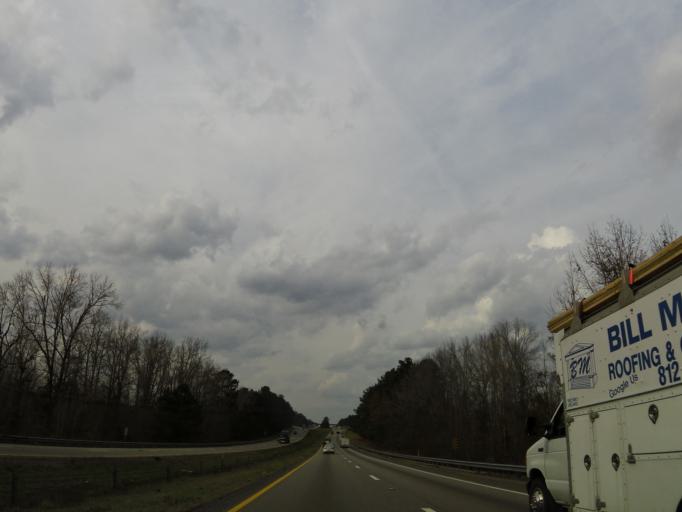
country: US
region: South Carolina
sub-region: Calhoun County
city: Saint Matthews
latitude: 33.6261
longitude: -80.8718
